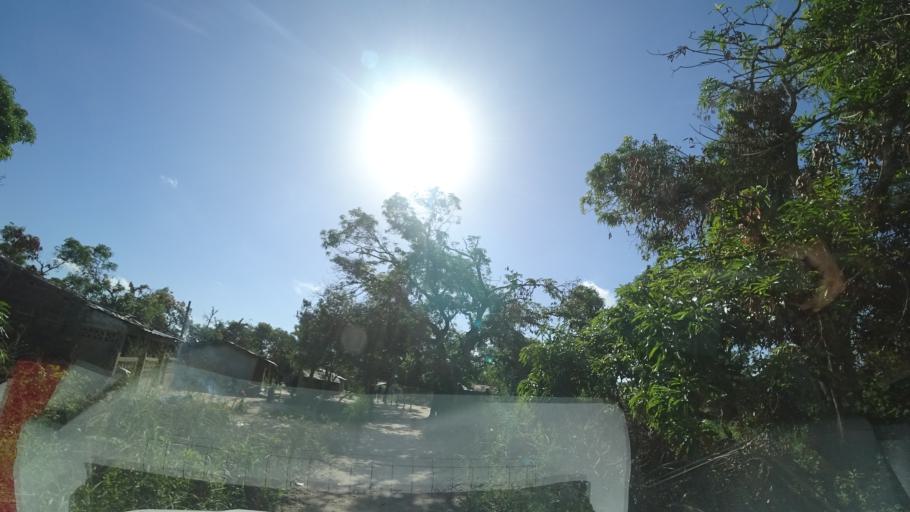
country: MZ
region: Sofala
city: Dondo
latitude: -19.4996
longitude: 34.5987
